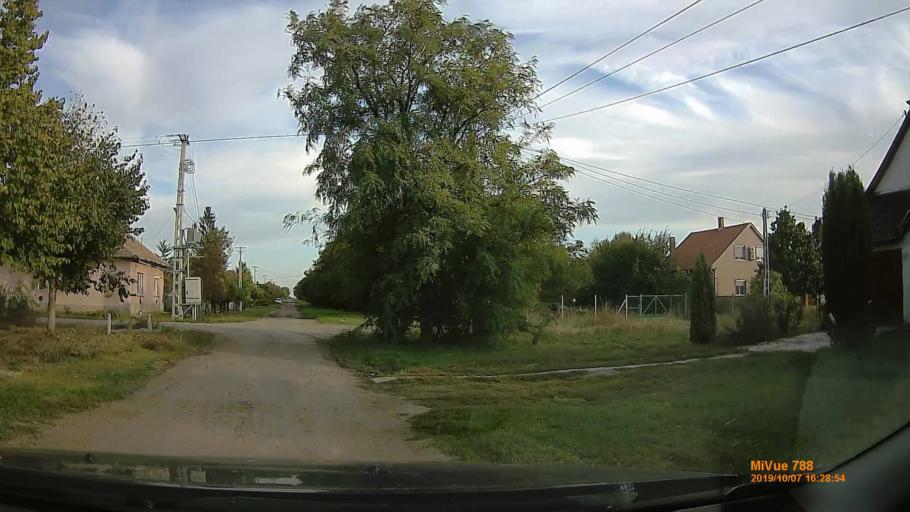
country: HU
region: Bekes
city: Szarvas
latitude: 46.8199
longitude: 20.6491
